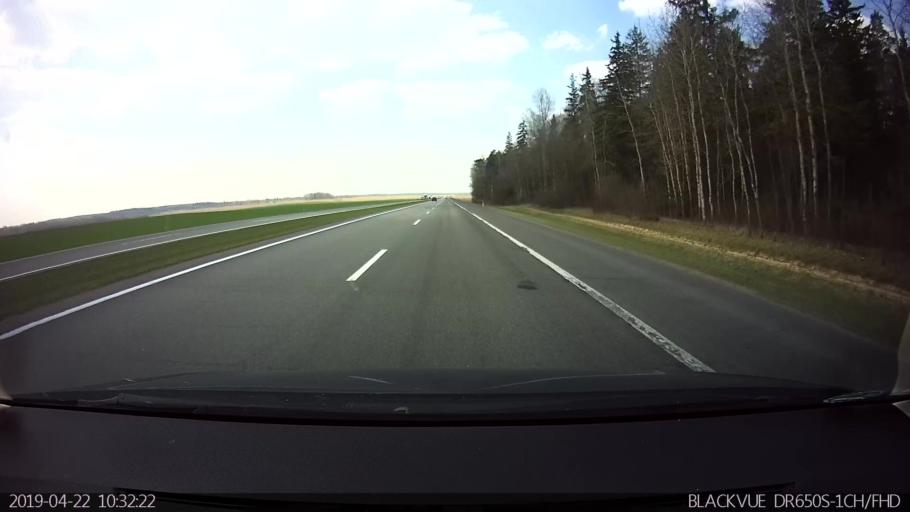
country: BY
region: Vitebsk
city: Talachyn
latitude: 54.4693
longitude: 29.7720
